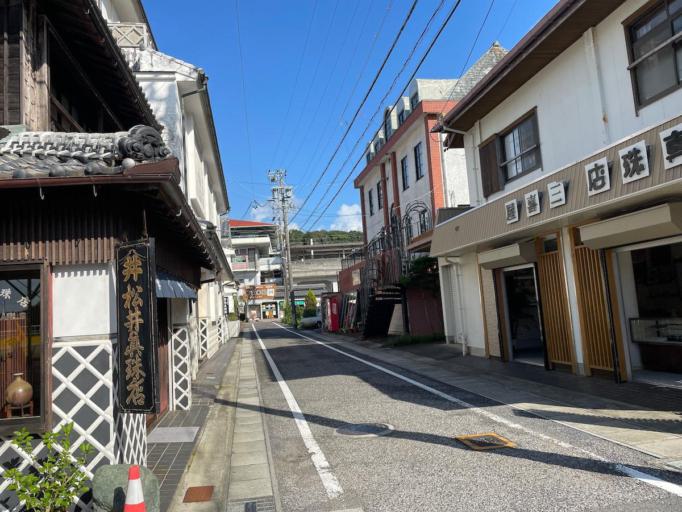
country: JP
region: Mie
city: Toba
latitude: 34.3076
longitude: 136.8191
